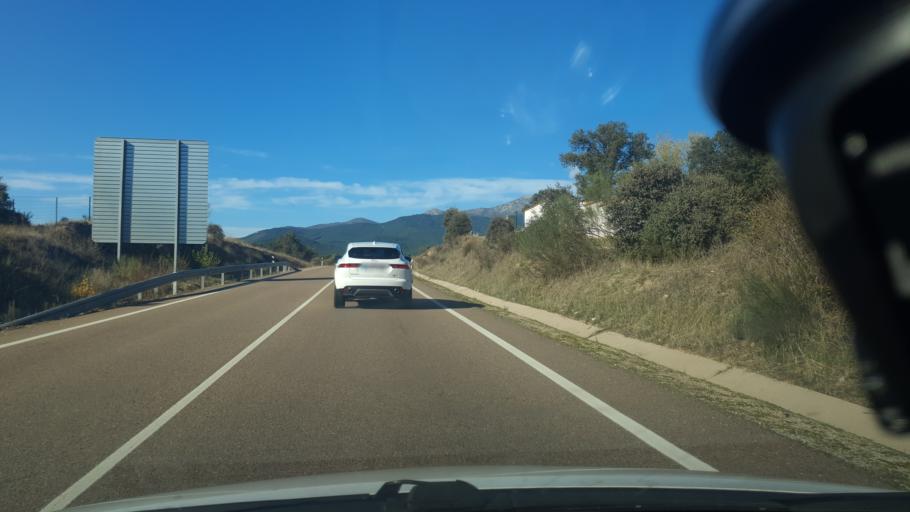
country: ES
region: Castille and Leon
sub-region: Provincia de Avila
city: Arenas de San Pedro
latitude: 40.1860
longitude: -5.0547
